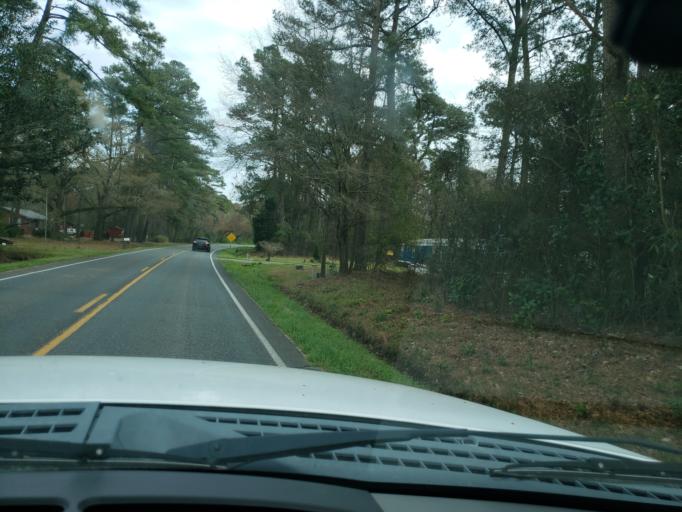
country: US
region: North Carolina
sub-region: Duplin County
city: Beulaville
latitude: 34.7580
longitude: -77.7906
